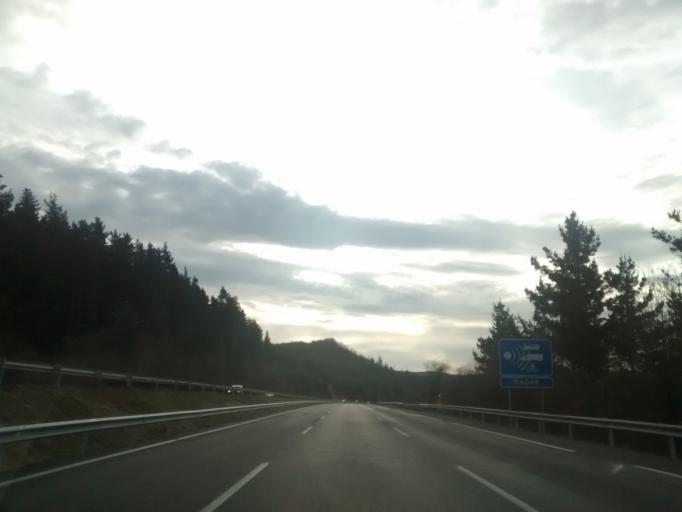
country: ES
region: Basque Country
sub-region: Provincia de Alava
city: Lezama
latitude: 43.0175
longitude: -2.9084
